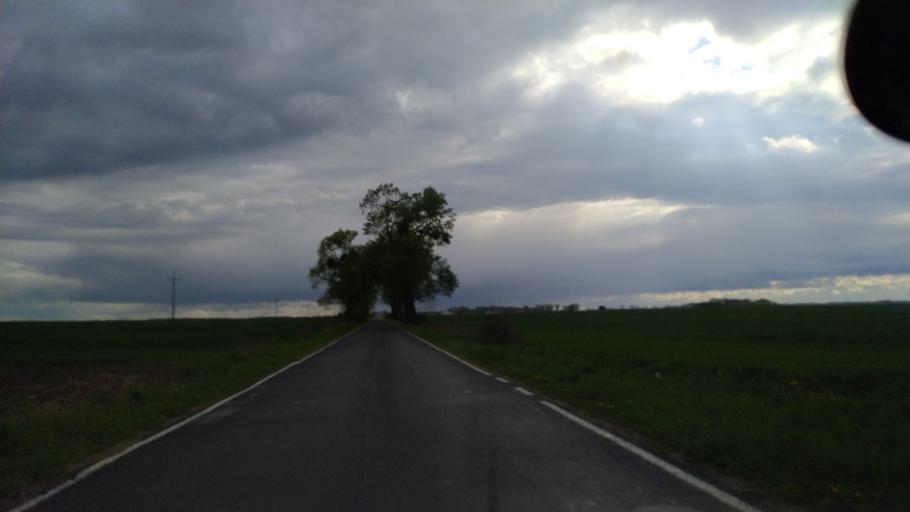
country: PL
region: Pomeranian Voivodeship
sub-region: Powiat starogardzki
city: Smetowo Graniczne
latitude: 53.7291
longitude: 18.6370
